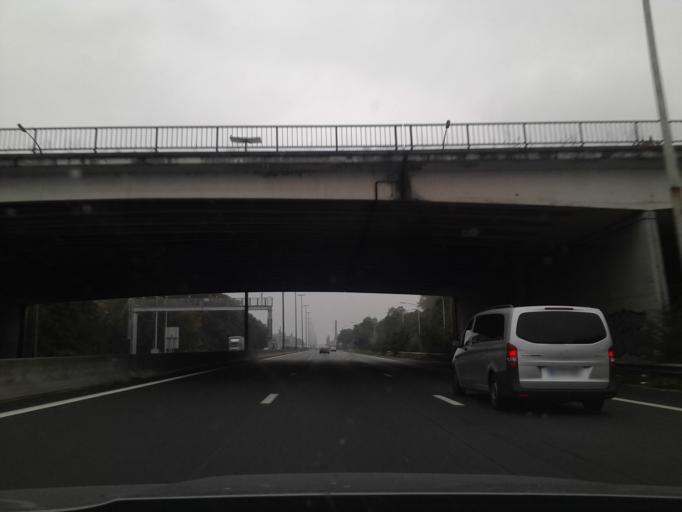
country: BE
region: Wallonia
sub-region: Province du Hainaut
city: Saint-Ghislain
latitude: 50.4527
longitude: 3.8286
